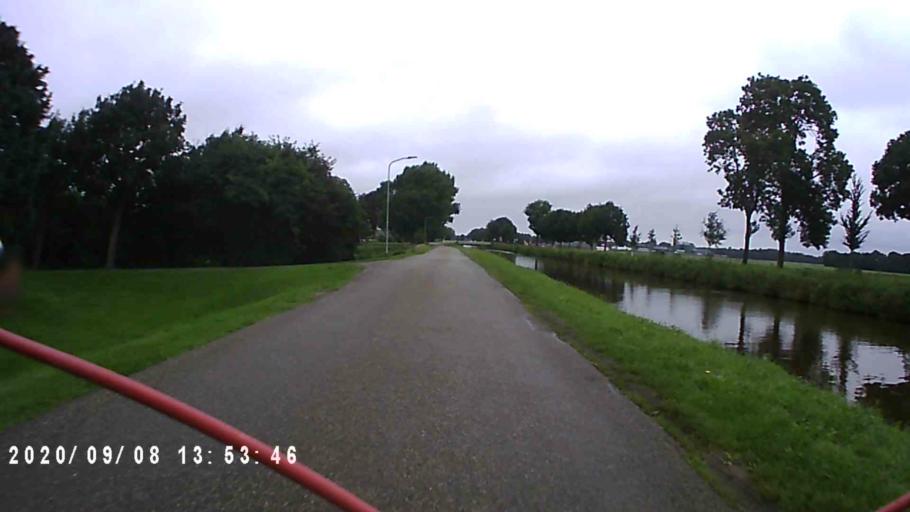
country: NL
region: Groningen
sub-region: Gemeente Veendam
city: Veendam
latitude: 53.1501
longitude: 6.8651
